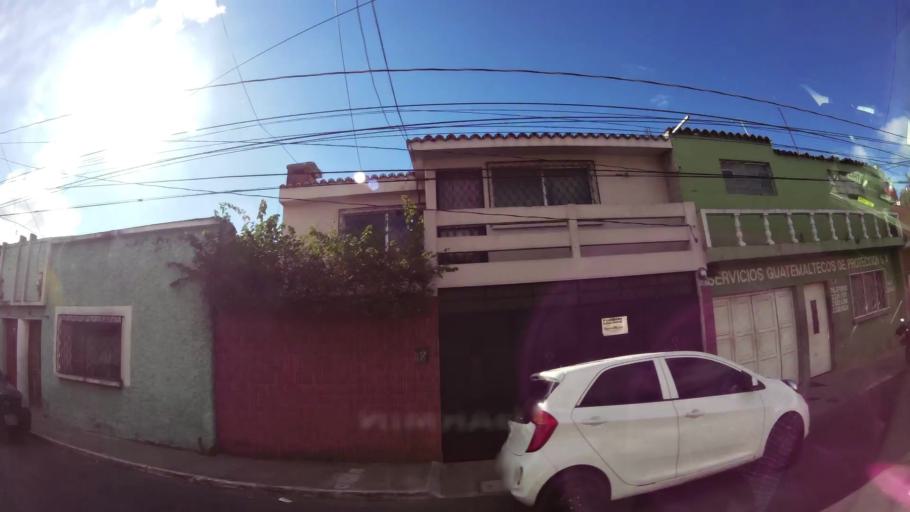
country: GT
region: Guatemala
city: Guatemala City
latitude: 14.6208
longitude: -90.5044
